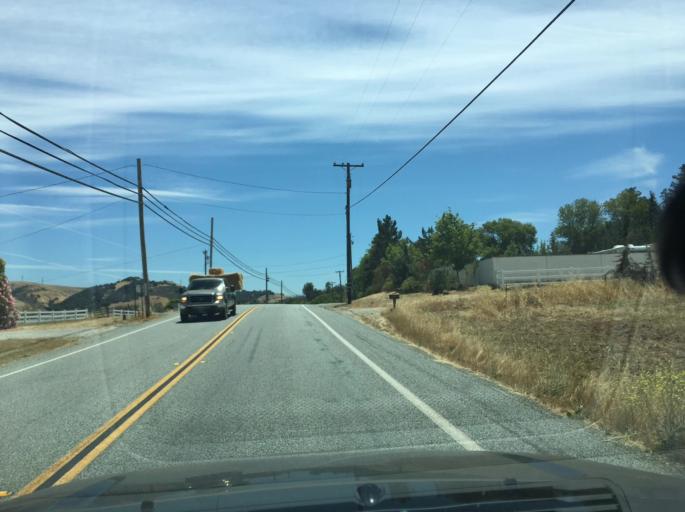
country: US
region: California
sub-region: Santa Clara County
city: Seven Trees
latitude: 37.1987
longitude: -121.8202
